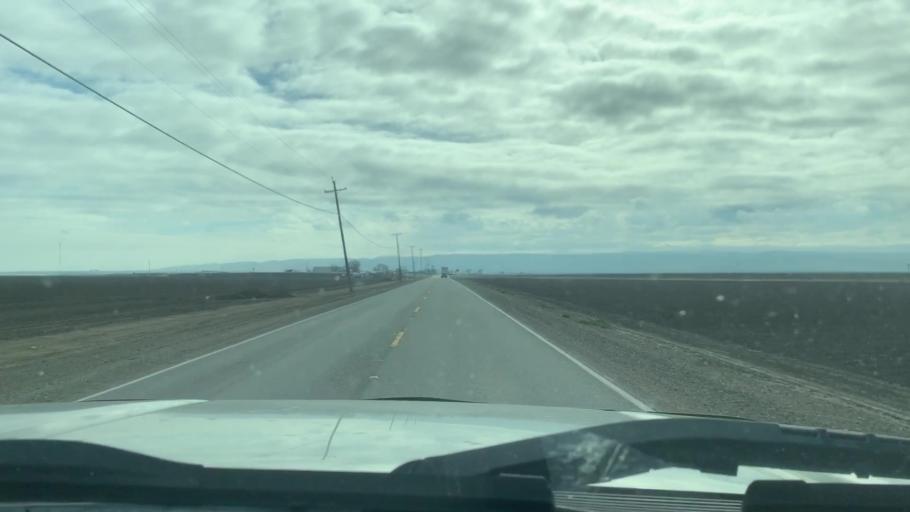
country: US
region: California
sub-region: Merced County
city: Los Banos
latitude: 36.9818
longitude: -120.8374
